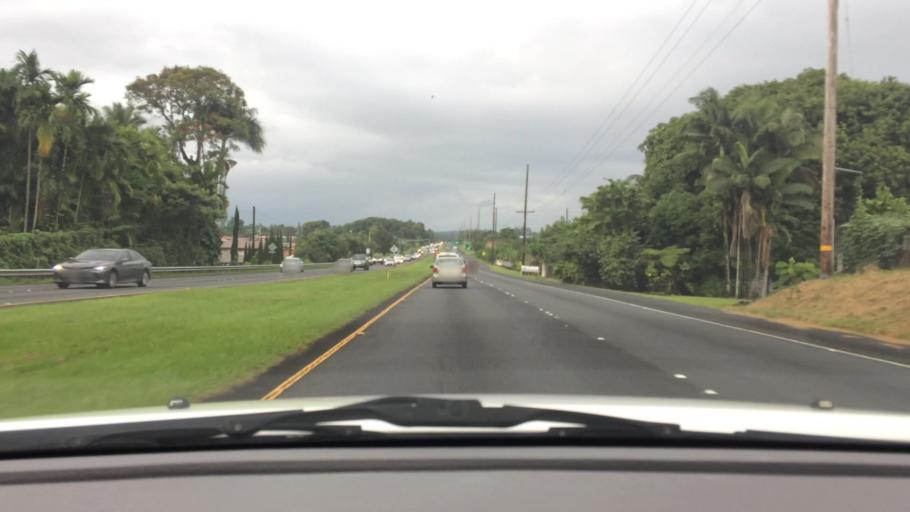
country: US
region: Hawaii
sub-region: Hawaii County
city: Hilo
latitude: 19.6883
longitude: -155.0658
